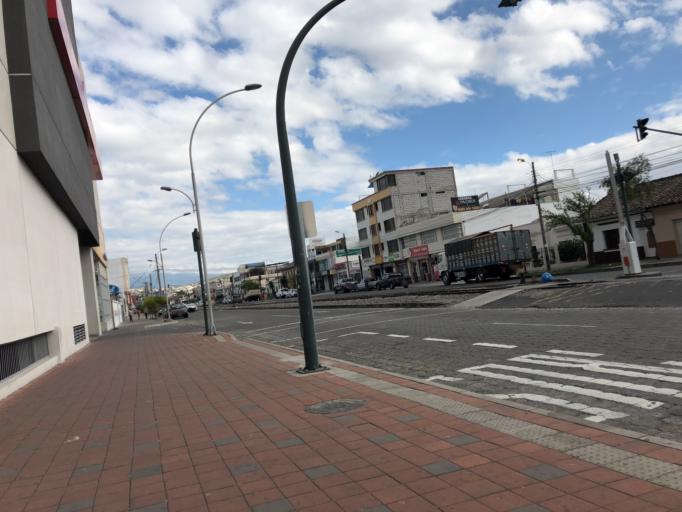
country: EC
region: Imbabura
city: Ibarra
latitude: 0.3494
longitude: -78.1253
